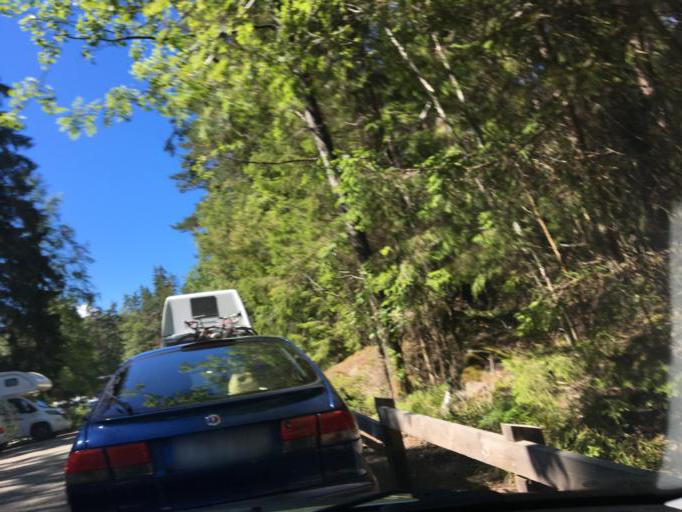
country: SE
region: Vaestra Goetaland
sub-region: Karlsborgs Kommun
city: Karlsborg
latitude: 58.7161
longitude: 14.5940
